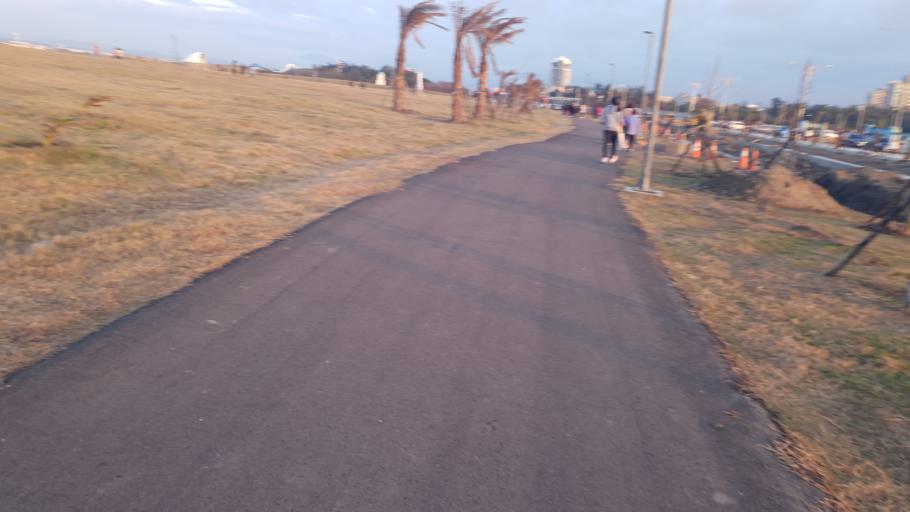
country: TW
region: Taiwan
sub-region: Hsinchu
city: Hsinchu
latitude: 24.8510
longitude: 120.9243
